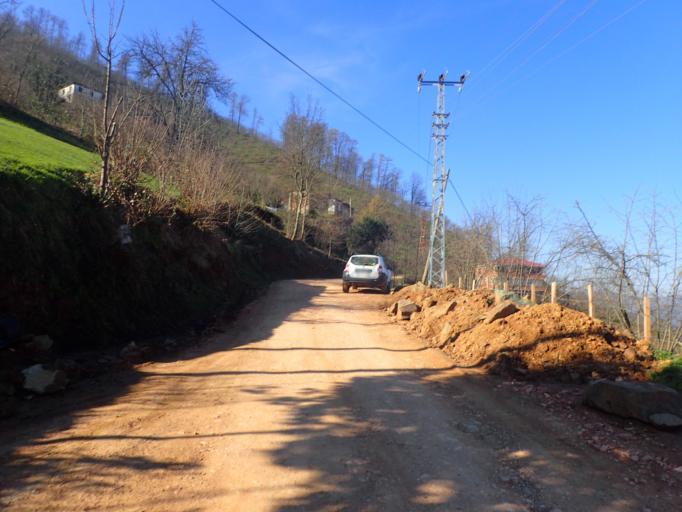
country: TR
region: Ordu
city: Camas
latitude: 40.8720
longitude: 37.5000
